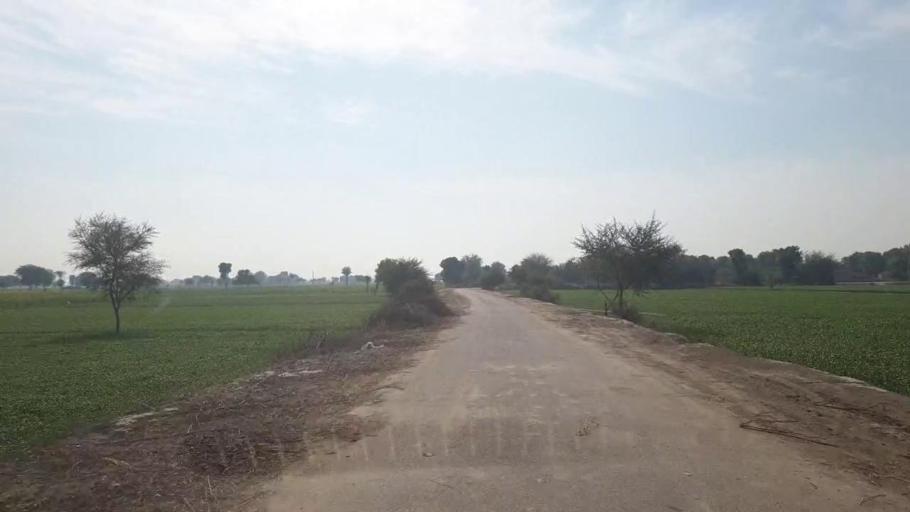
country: PK
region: Sindh
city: Shahpur Chakar
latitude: 26.1533
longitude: 68.5151
